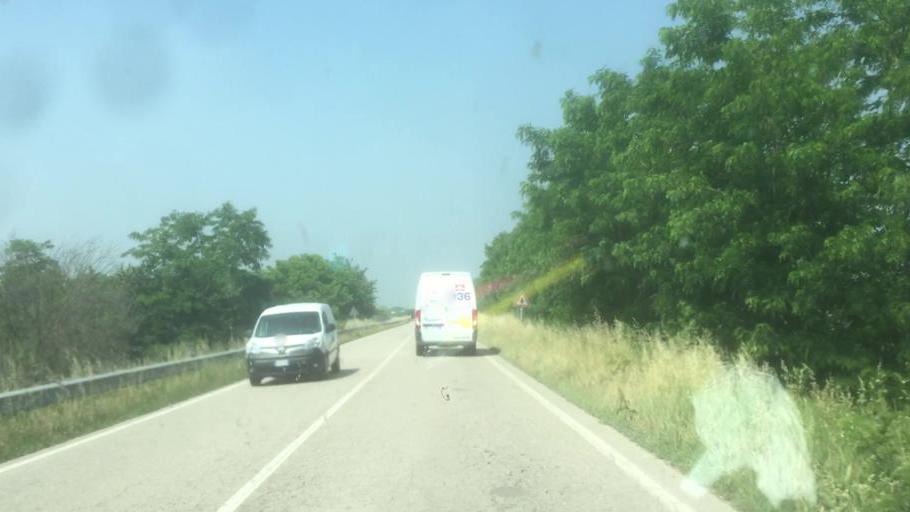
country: IT
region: Lombardy
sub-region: Provincia di Mantova
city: Revere
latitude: 45.0346
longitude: 11.1594
